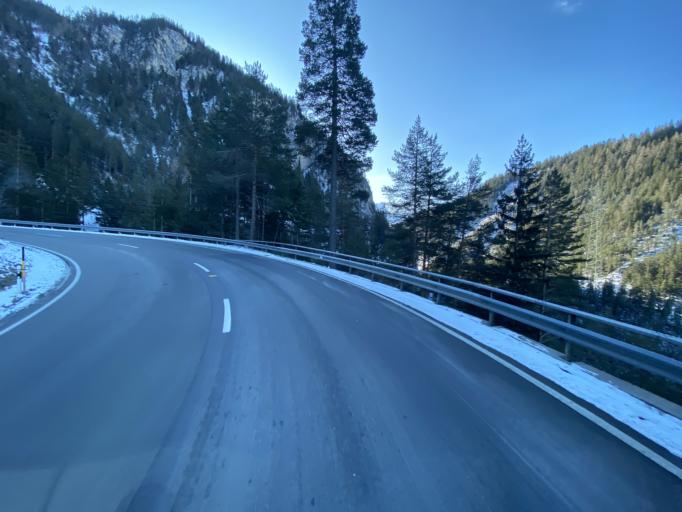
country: CH
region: Grisons
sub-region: Albula District
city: Tiefencastel
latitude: 46.6425
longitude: 9.5842
